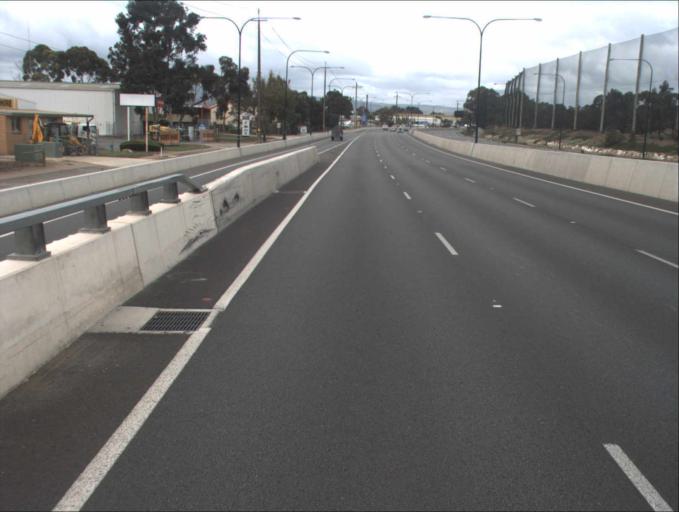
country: AU
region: South Australia
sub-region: Charles Sturt
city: Woodville North
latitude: -34.8612
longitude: 138.5679
